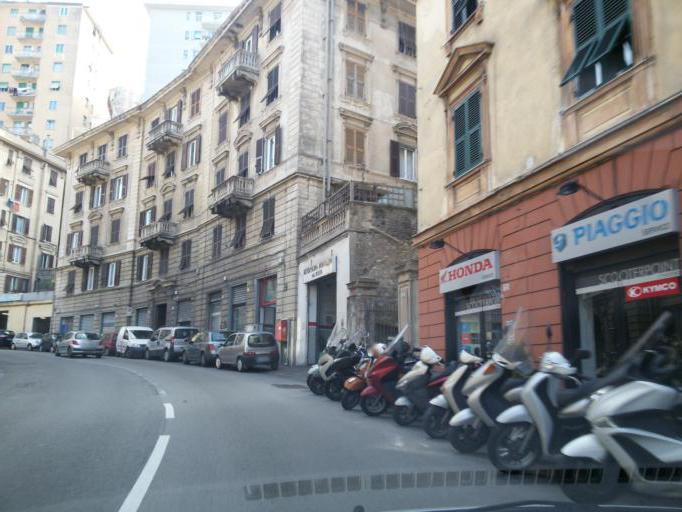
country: IT
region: Liguria
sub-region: Provincia di Genova
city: Genoa
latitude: 44.4185
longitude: 8.9459
